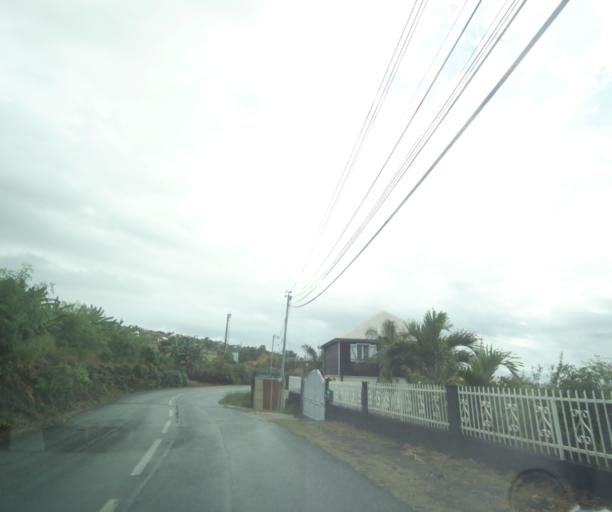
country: RE
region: Reunion
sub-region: Reunion
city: Saint-Paul
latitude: -21.0156
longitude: 55.3064
